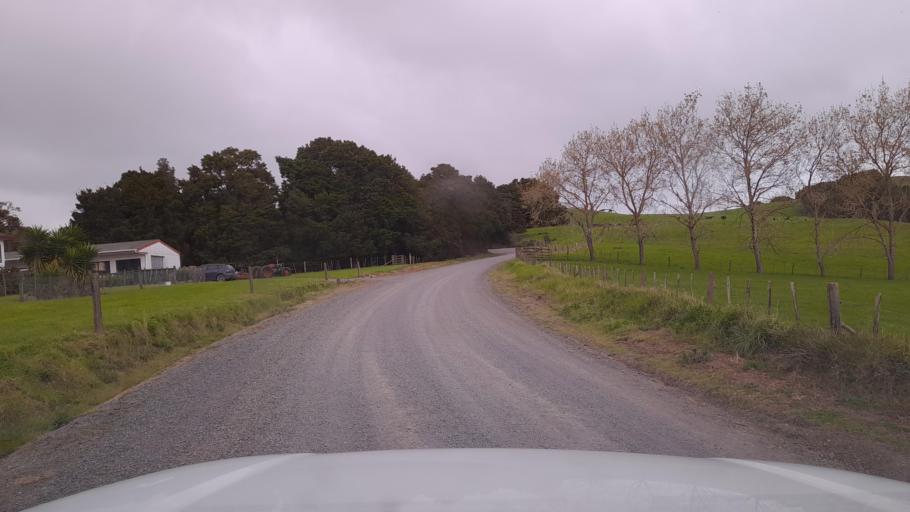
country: NZ
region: Northland
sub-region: Whangarei
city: Maungatapere
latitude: -35.6321
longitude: 174.1933
